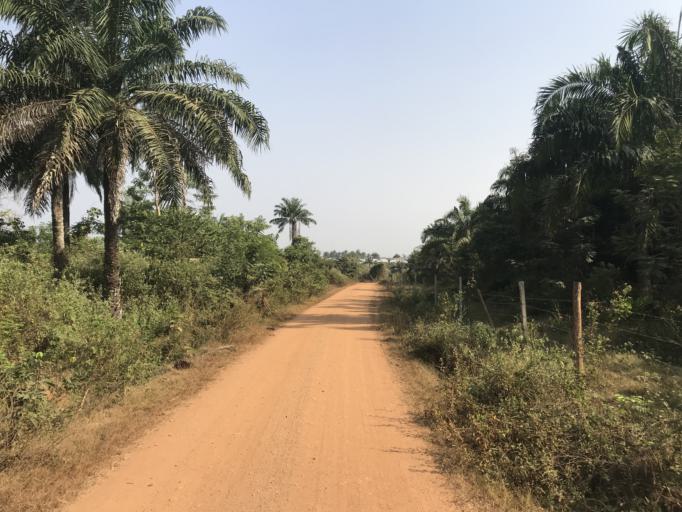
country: NG
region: Osun
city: Olupona
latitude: 7.6150
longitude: 4.1523
